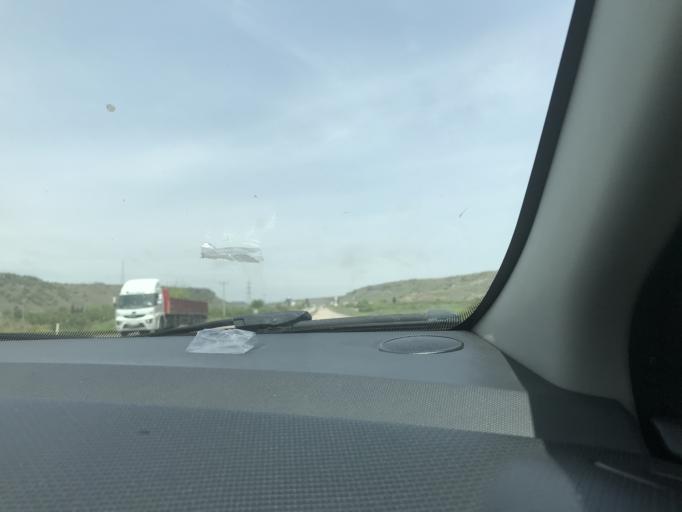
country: TR
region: Osmaniye
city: Toprakkale
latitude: 37.0092
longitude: 36.1372
